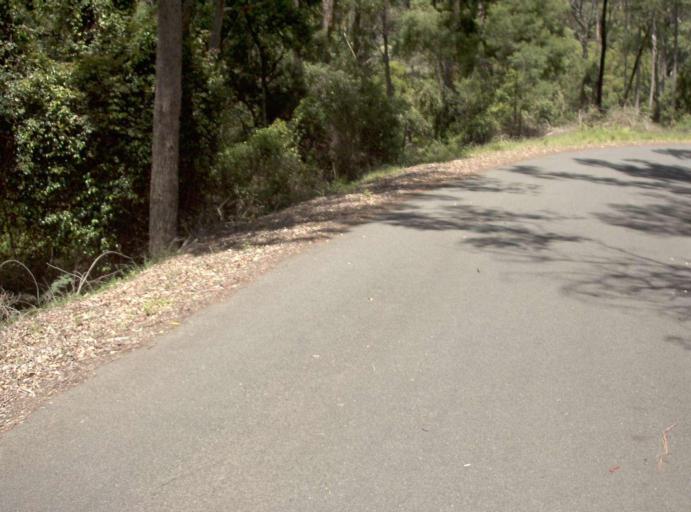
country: AU
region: New South Wales
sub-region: Bombala
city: Bombala
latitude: -37.4778
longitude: 148.9266
